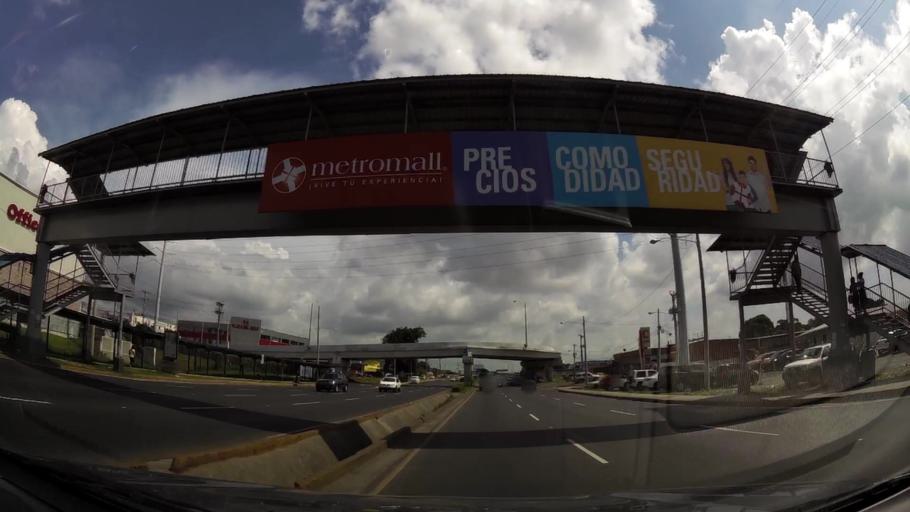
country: PA
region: Panama
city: San Miguelito
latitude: 9.0486
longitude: -79.4608
